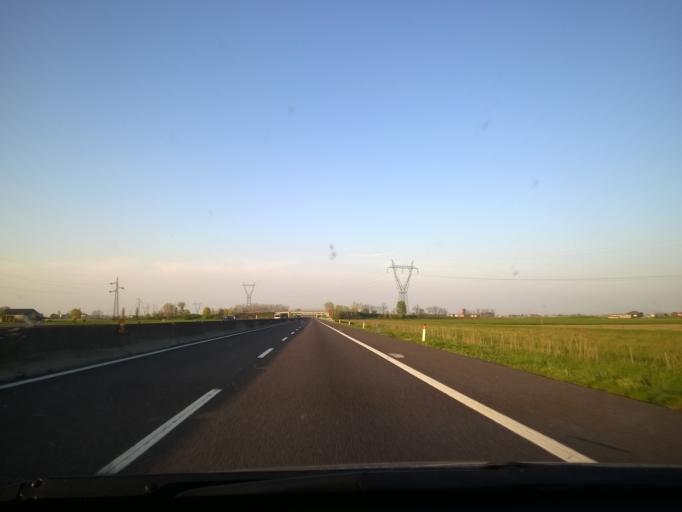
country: IT
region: Emilia-Romagna
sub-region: Provincia di Ferrara
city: Gallo
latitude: 44.7708
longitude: 11.5427
